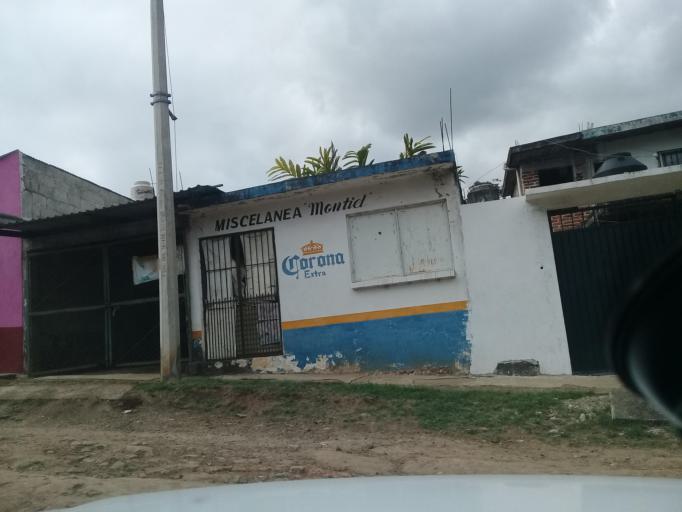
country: MX
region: Veracruz
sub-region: Xalapa
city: Fraccionamiento las Fuentes
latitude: 19.4745
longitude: -96.8776
